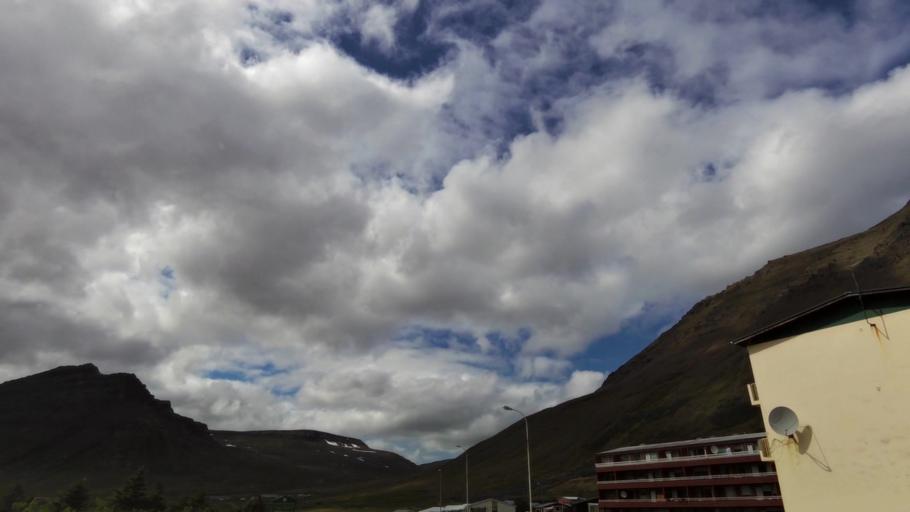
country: IS
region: Westfjords
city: Isafjoerdur
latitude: 66.1585
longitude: -23.2603
